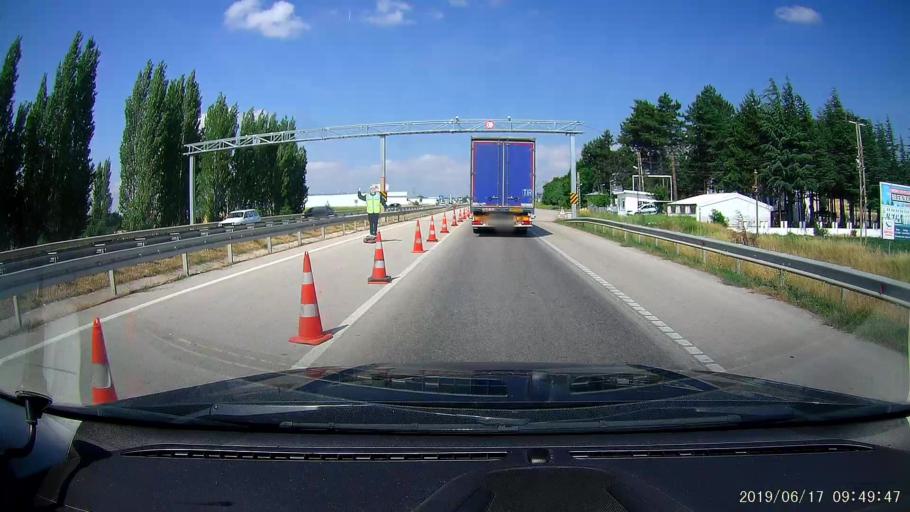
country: TR
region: Amasya
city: Merzifon
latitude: 40.8721
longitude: 35.5206
